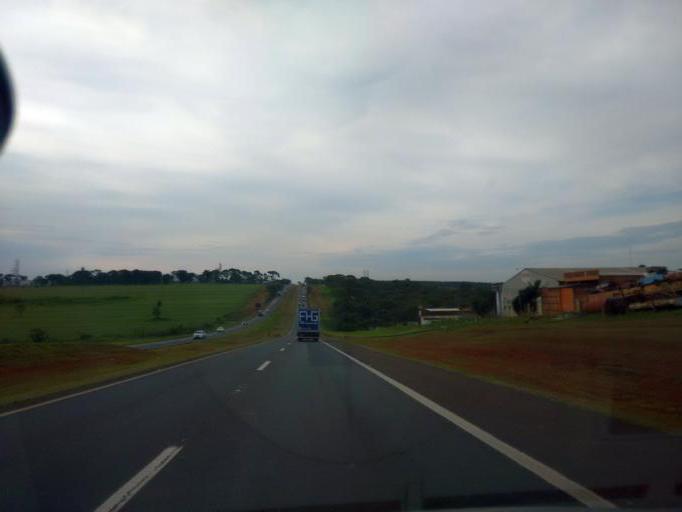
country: BR
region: Sao Paulo
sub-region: Araraquara
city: Araraquara
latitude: -21.7952
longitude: -48.2103
